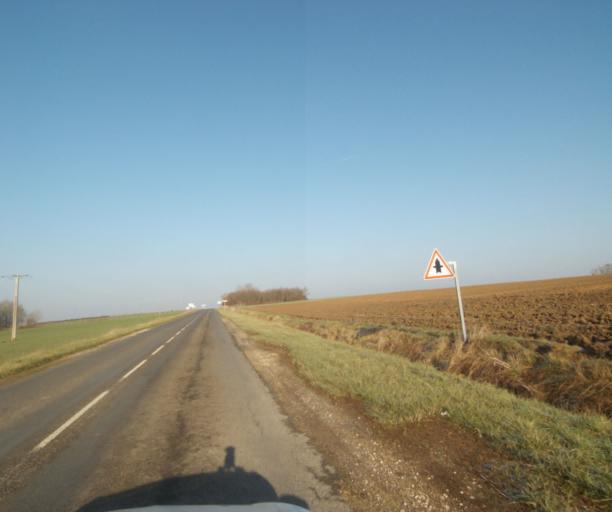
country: FR
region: Champagne-Ardenne
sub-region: Departement de la Haute-Marne
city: Montier-en-Der
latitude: 48.4930
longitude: 4.7558
